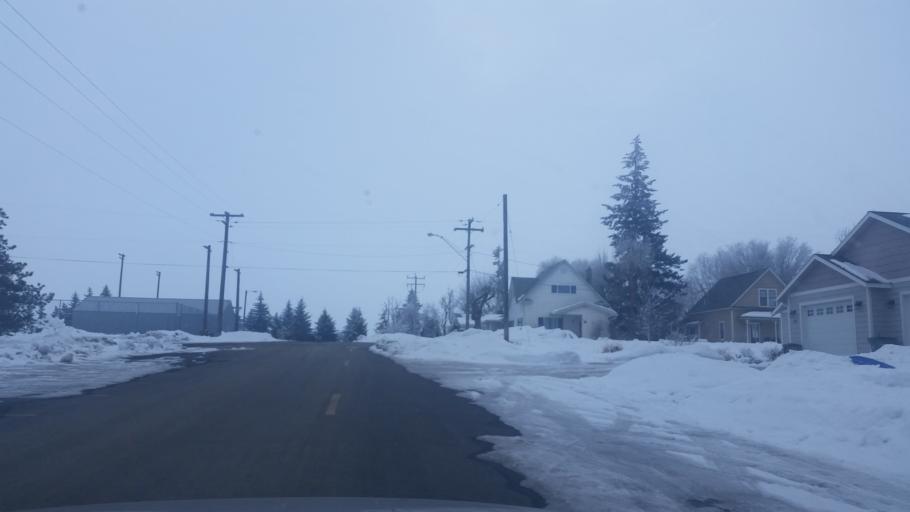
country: US
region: Washington
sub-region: Spokane County
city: Medical Lake
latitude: 47.6668
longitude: -117.8779
